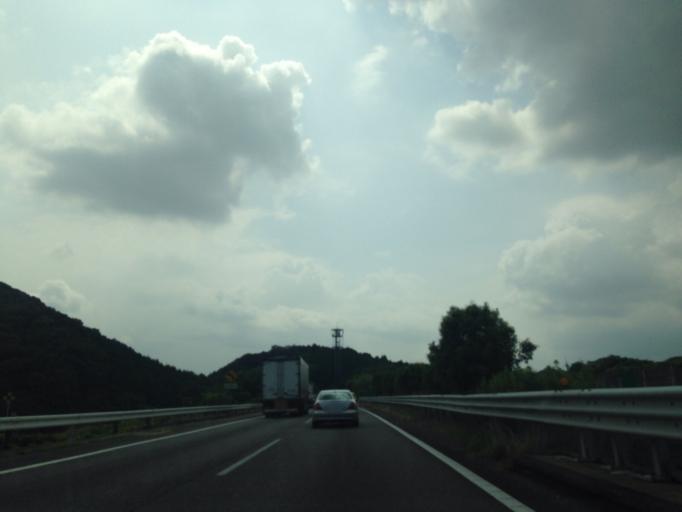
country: JP
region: Aichi
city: Kozakai-cho
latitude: 34.8508
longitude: 137.3488
